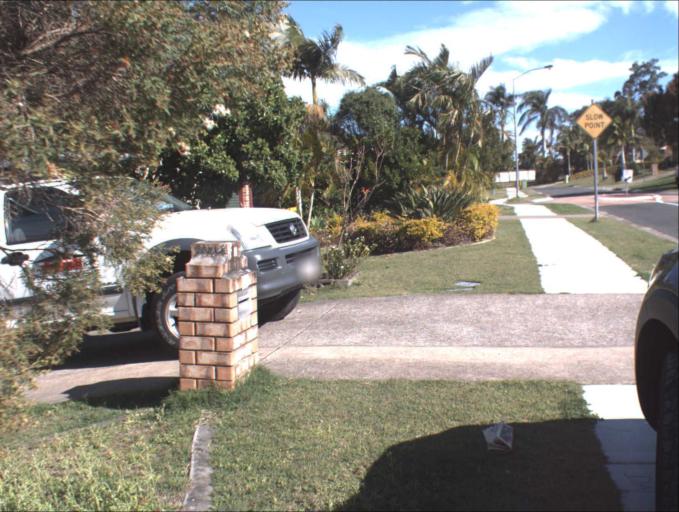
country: AU
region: Queensland
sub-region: Logan
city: Logan Reserve
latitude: -27.6953
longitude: 153.0788
